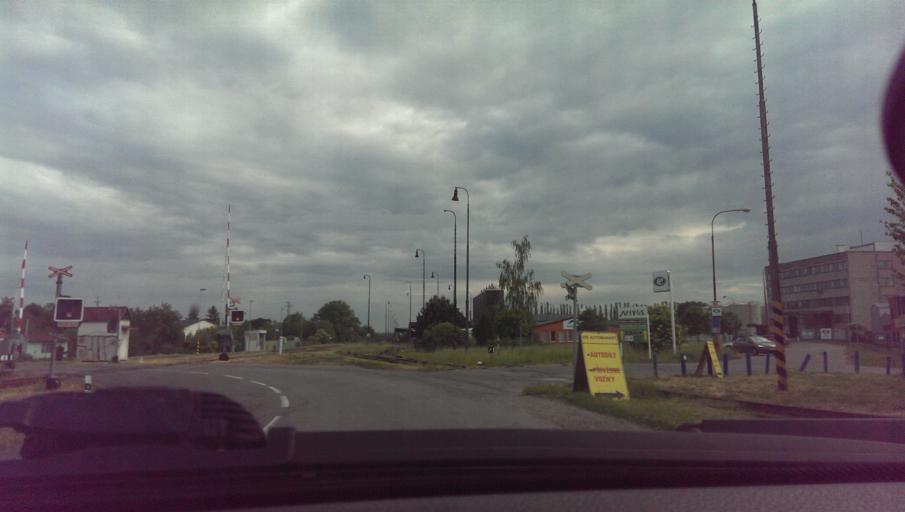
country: CZ
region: Zlin
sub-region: Okres Kromeriz
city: Kromeriz
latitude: 49.2831
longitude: 17.4033
